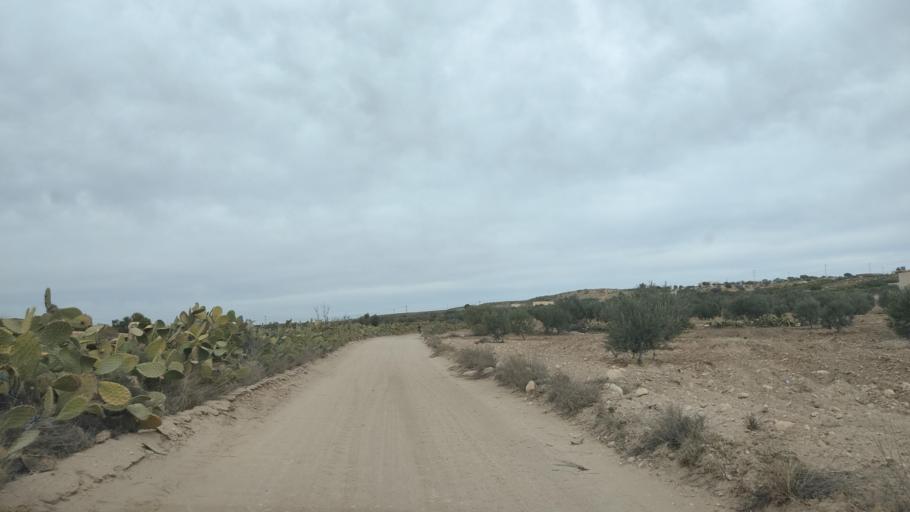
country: TN
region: Al Qasrayn
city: Kasserine
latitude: 35.2439
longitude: 8.9175
